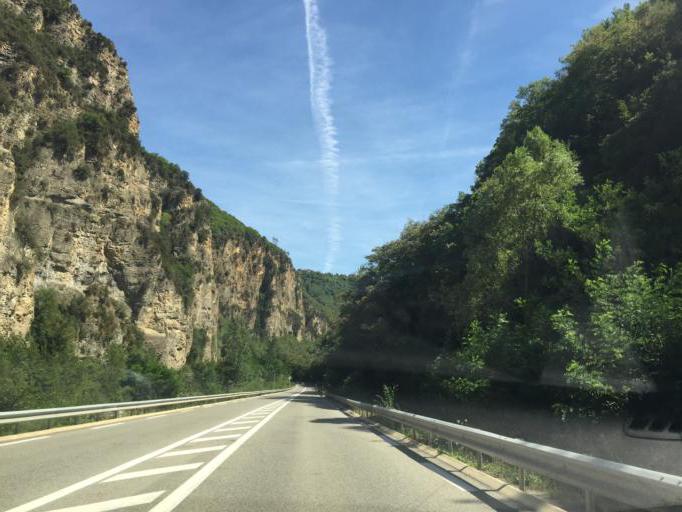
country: FR
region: Provence-Alpes-Cote d'Azur
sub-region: Departement des Alpes-Maritimes
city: Saint-Martin-Vesubie
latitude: 44.0096
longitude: 7.1325
